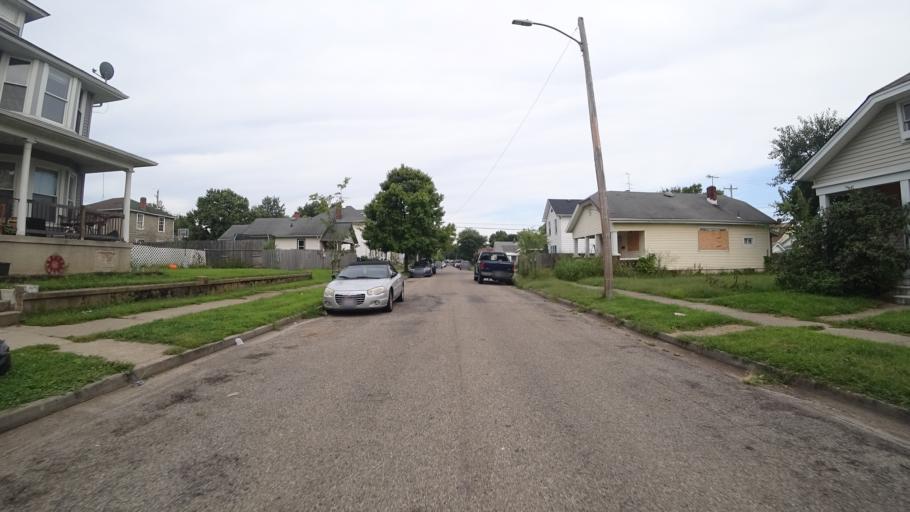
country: US
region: Ohio
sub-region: Butler County
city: Hamilton
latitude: 39.3962
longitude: -84.5454
